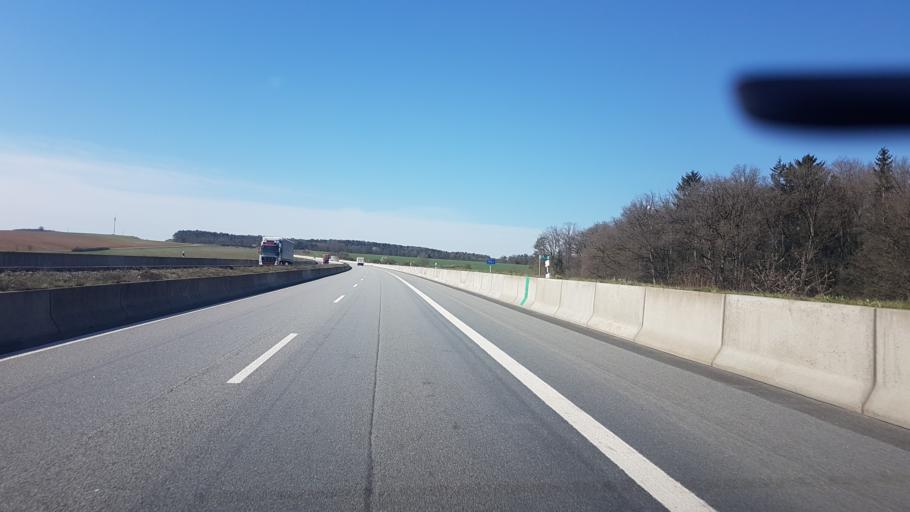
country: DE
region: Bavaria
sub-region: Regierungsbezirk Unterfranken
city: Rannungen
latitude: 50.1893
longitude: 10.2028
